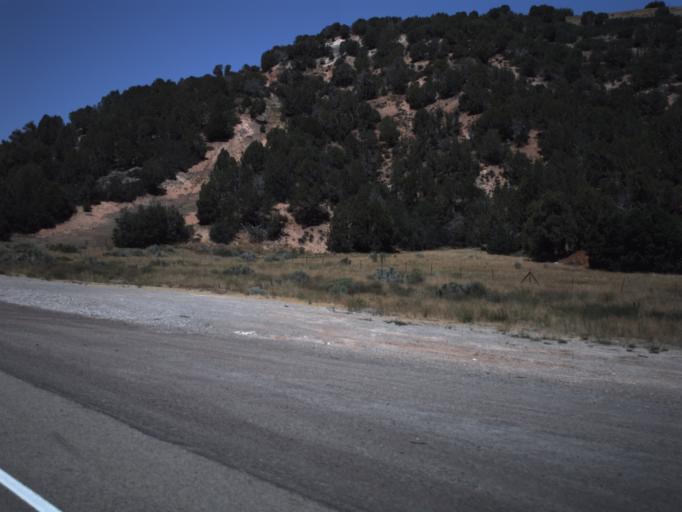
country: US
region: Utah
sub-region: Utah County
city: Mapleton
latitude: 40.0010
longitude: -111.4847
